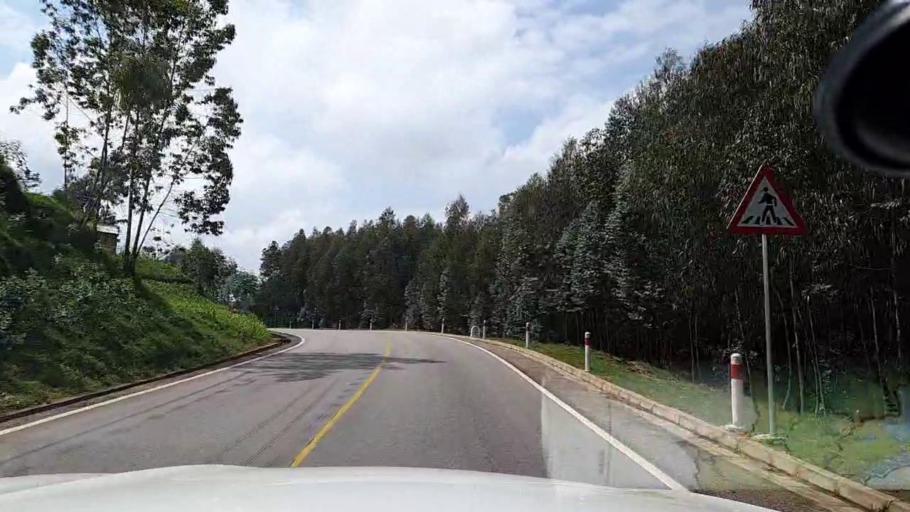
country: RW
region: Southern Province
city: Nzega
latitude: -2.4932
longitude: 29.5067
